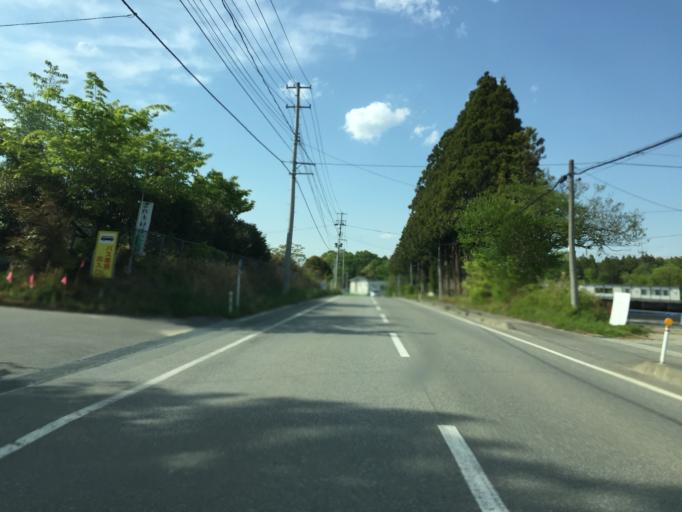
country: JP
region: Fukushima
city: Namie
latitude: 37.3758
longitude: 140.9585
